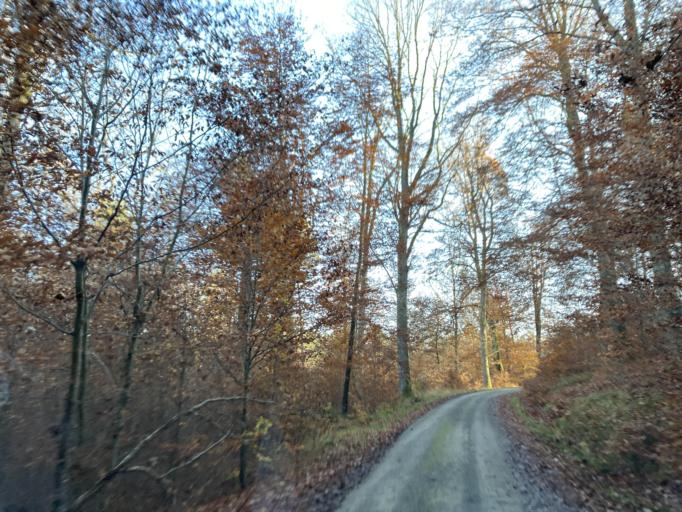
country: DE
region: Baden-Wuerttemberg
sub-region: Tuebingen Region
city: Tuebingen
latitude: 48.5551
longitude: 9.0127
